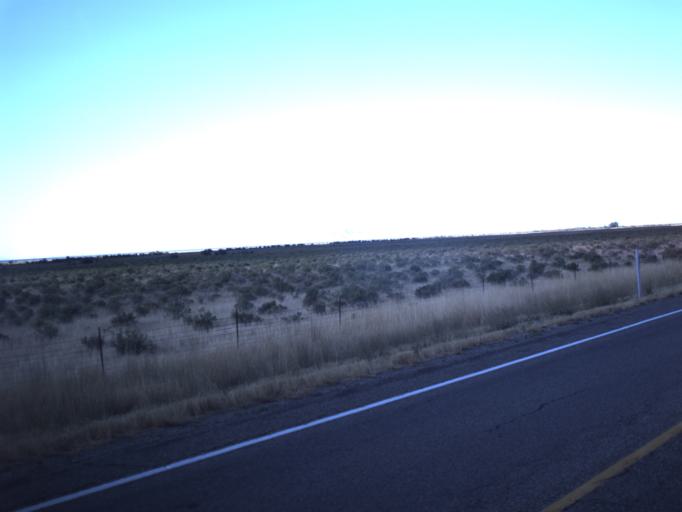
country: US
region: Utah
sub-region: Tooele County
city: Erda
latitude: 40.6080
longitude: -112.3834
